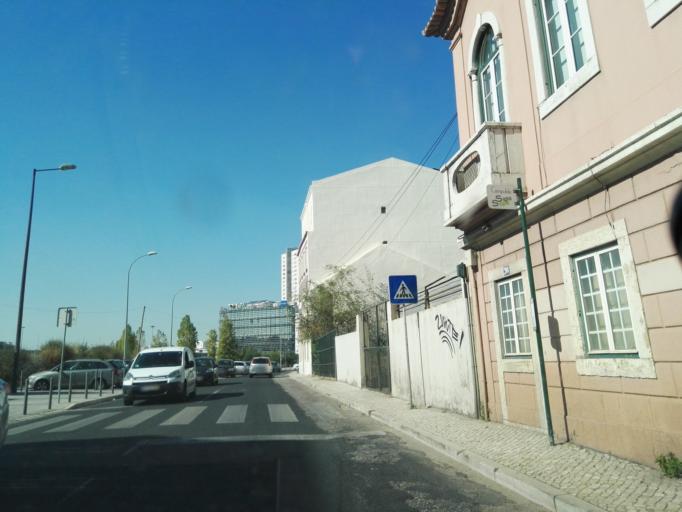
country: PT
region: Lisbon
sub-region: Lisbon
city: Lisbon
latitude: 38.7354
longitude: -9.1655
